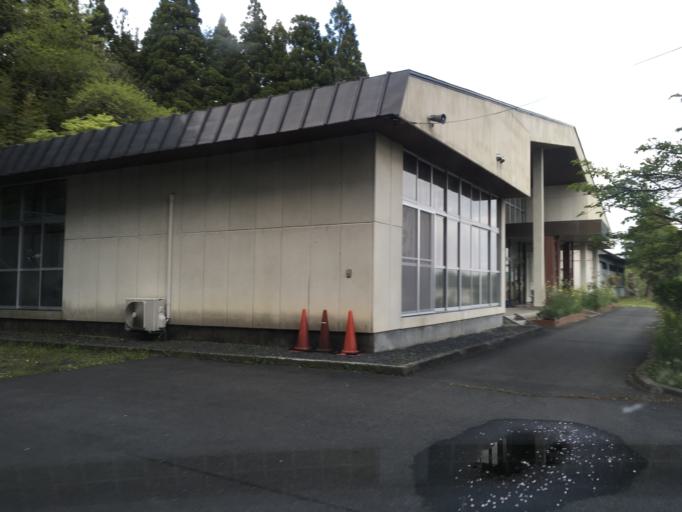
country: JP
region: Iwate
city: Ichinoseki
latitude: 38.8118
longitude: 141.1755
